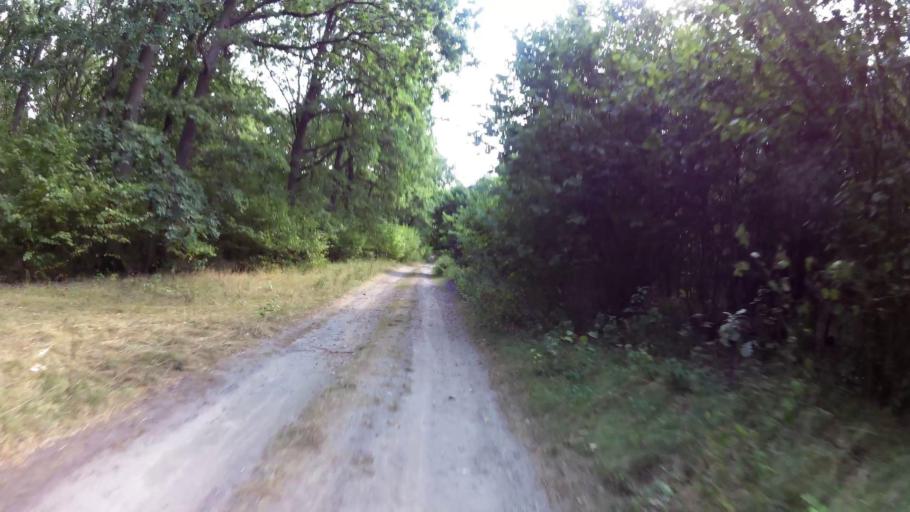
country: PL
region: West Pomeranian Voivodeship
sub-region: Powiat gryfinski
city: Moryn
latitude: 52.8786
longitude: 14.4292
